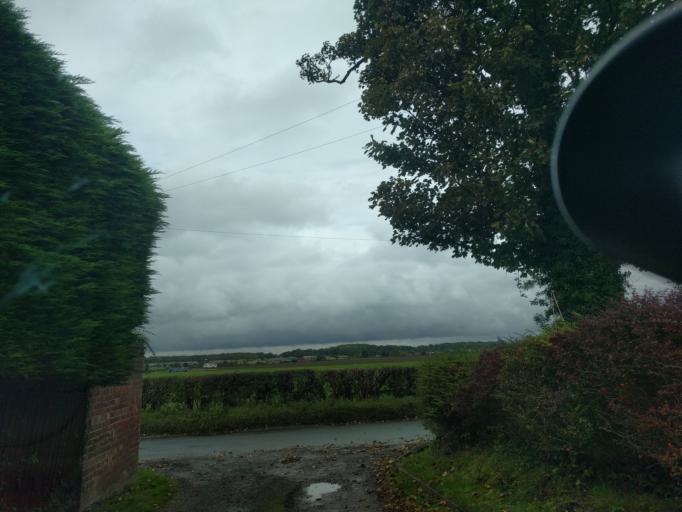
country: GB
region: England
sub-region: North Yorkshire
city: Bedale
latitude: 54.3427
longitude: -1.5857
